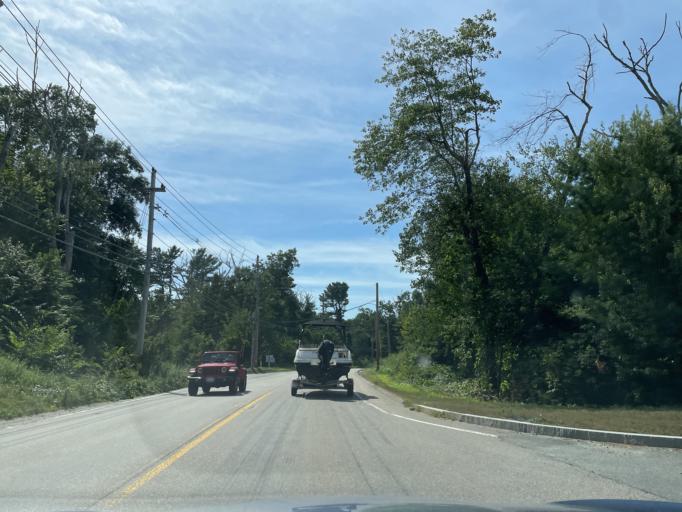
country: US
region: Massachusetts
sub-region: Norfolk County
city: Wrentham
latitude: 42.0732
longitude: -71.3557
